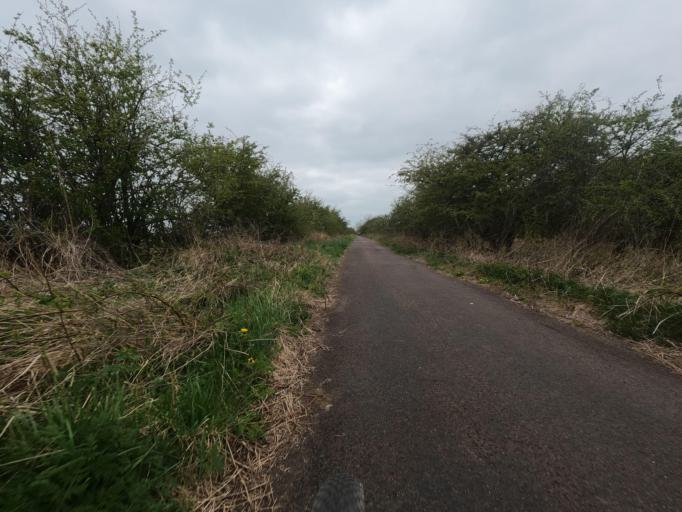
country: GB
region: England
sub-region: Newcastle upon Tyne
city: Dinnington
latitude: 55.0566
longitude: -1.6984
